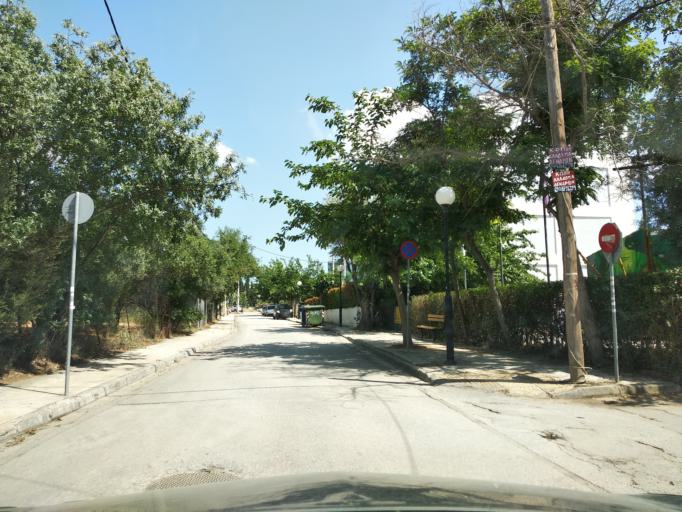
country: GR
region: Attica
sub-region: Nomarchia Athinas
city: Marousi
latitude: 38.0395
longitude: 23.7983
